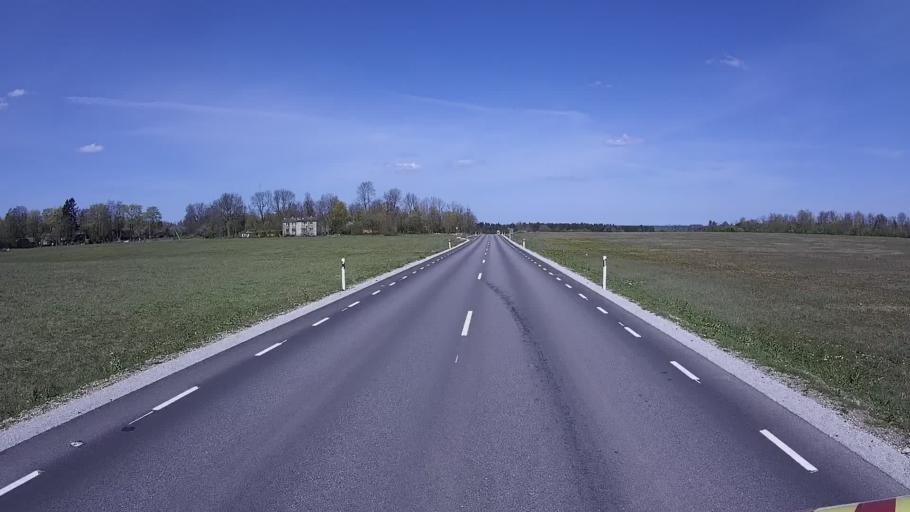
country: EE
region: Harju
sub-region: Paldiski linn
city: Paldiski
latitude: 59.2079
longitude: 24.0953
